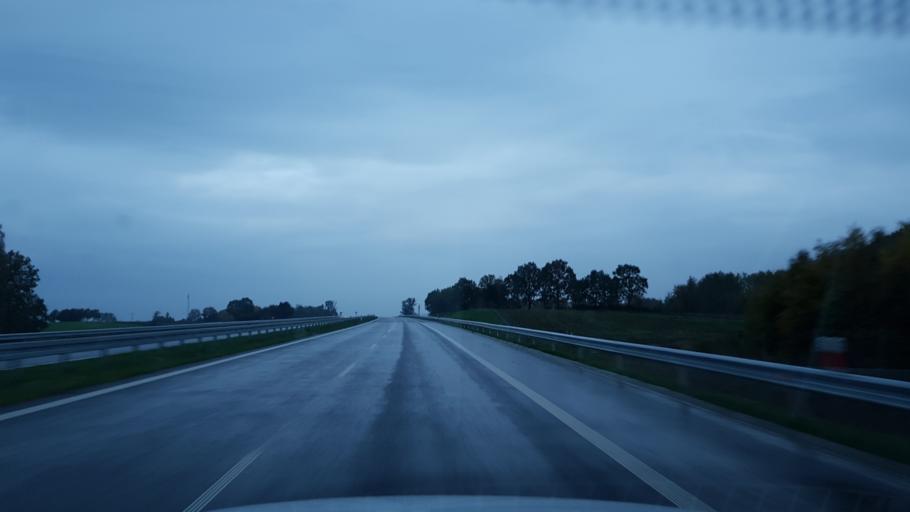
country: PL
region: West Pomeranian Voivodeship
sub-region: Powiat kolobrzeski
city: Ryman
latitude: 54.0136
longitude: 15.4749
